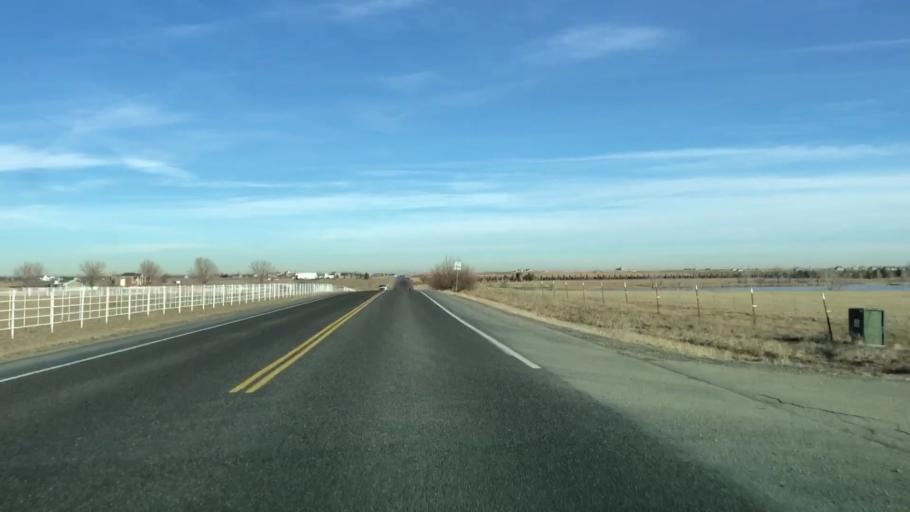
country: US
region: Colorado
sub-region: Weld County
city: Windsor
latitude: 40.4216
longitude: -104.9443
